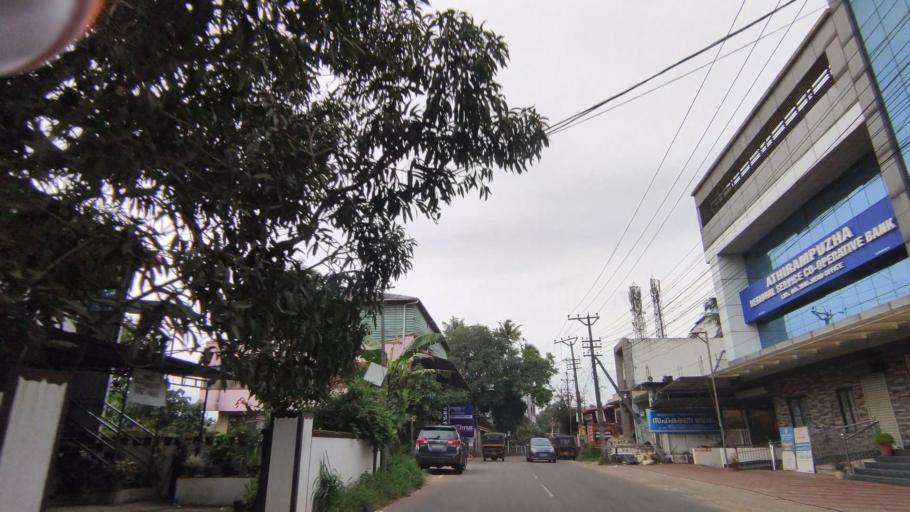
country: IN
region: Kerala
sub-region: Kottayam
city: Kottayam
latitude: 9.6664
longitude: 76.5323
